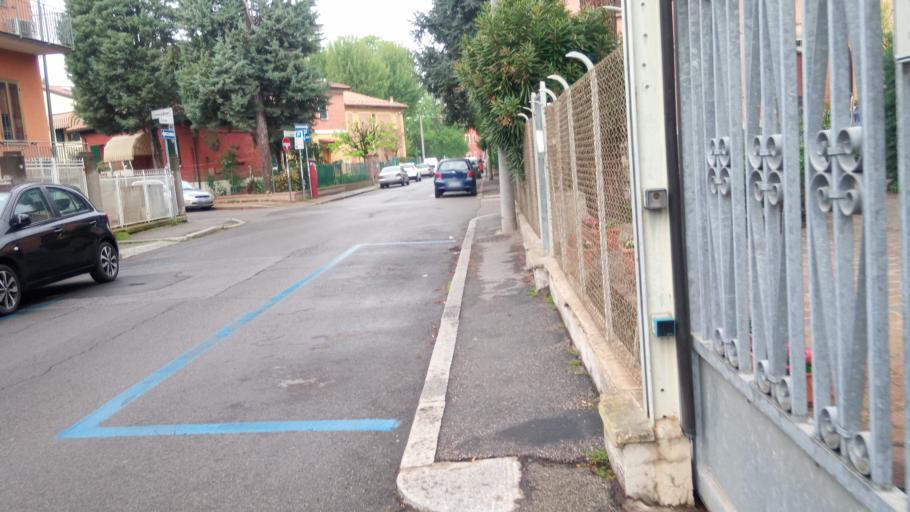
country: IT
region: Emilia-Romagna
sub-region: Provincia di Bologna
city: Bologna
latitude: 44.5186
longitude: 11.3412
